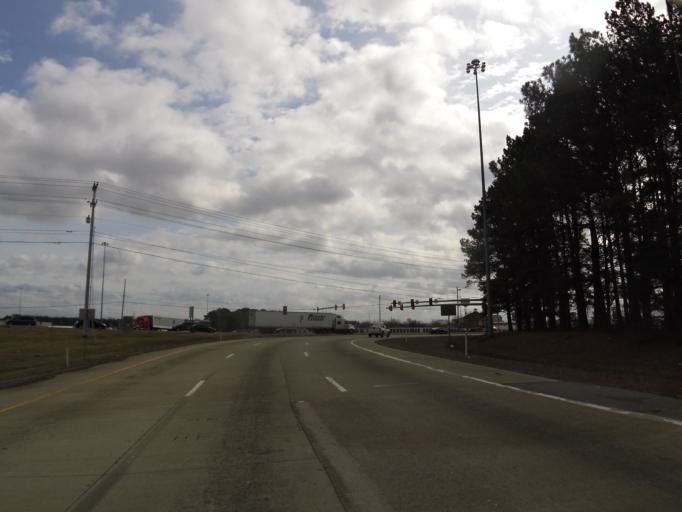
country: US
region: Tennessee
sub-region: Rutherford County
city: Murfreesboro
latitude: 35.8105
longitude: -86.3981
